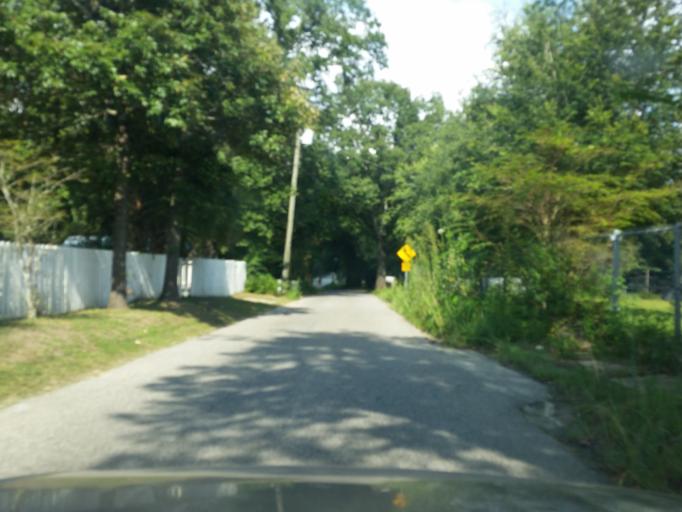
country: US
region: Florida
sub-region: Escambia County
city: Ferry Pass
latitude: 30.4976
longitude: -87.2122
